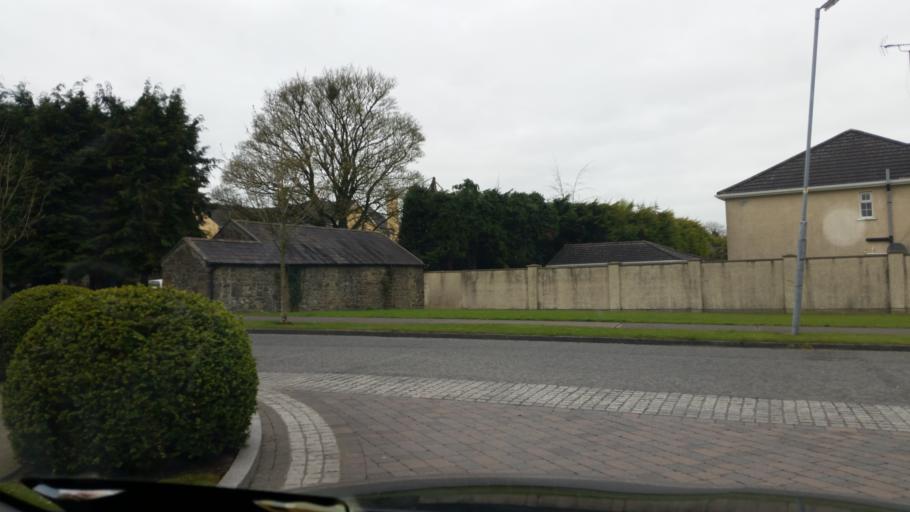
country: IE
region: Leinster
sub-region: An Iarmhi
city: An Muileann gCearr
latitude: 53.5237
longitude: -7.3058
